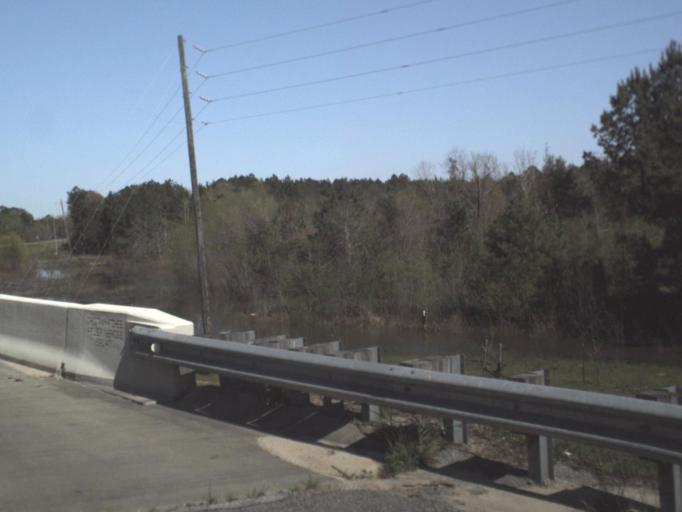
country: US
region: Florida
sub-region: Holmes County
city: Bonifay
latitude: 30.7774
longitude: -85.8410
